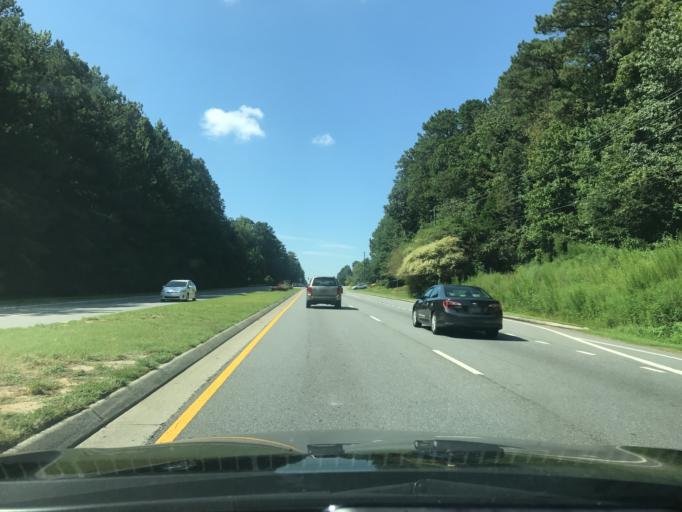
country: US
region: Georgia
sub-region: Gwinnett County
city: Berkeley Lake
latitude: 33.9938
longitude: -84.2065
